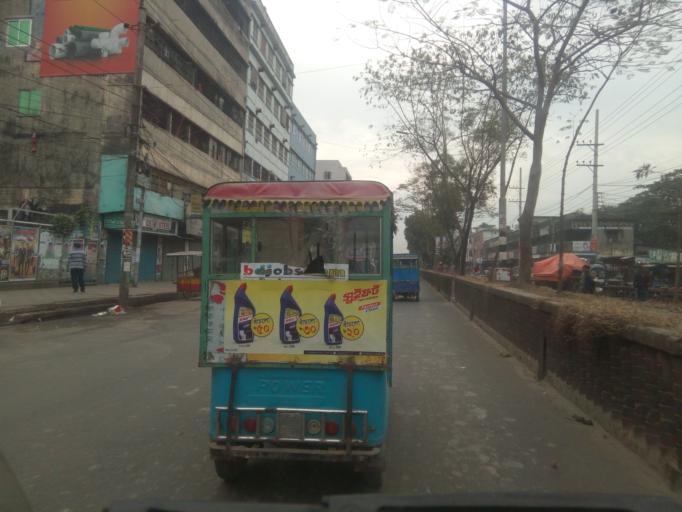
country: BD
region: Dhaka
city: Narayanganj
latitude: 23.6123
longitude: 90.5023
